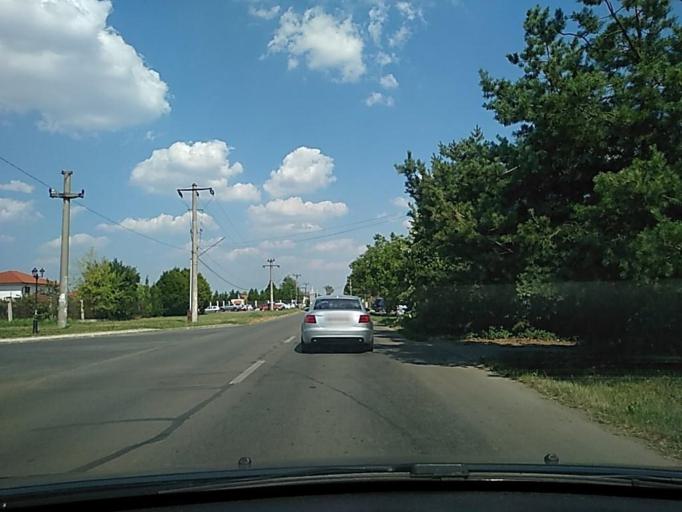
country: RO
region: Ilfov
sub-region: Comuna Clinceni
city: Olteni
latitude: 44.4034
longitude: 25.9509
